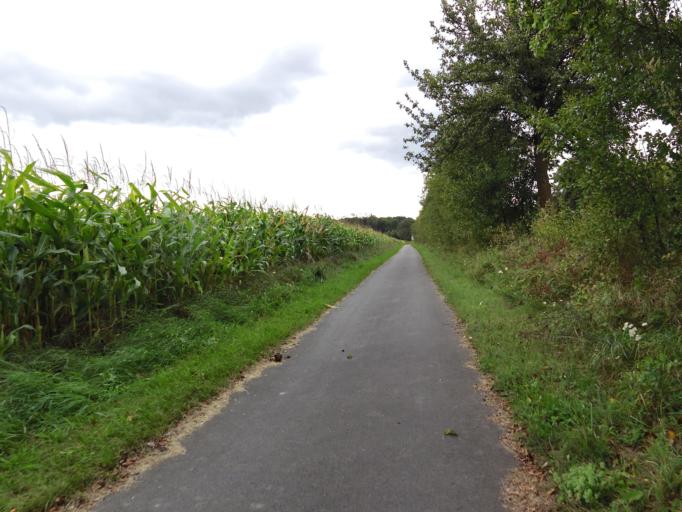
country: DE
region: Saxony-Anhalt
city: Arneburg
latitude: 52.6226
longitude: 12.0011
